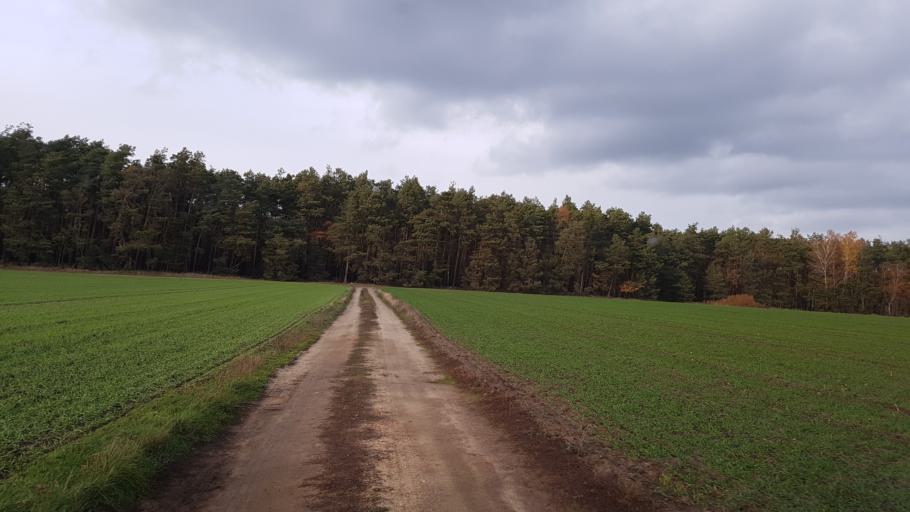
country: DE
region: Brandenburg
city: Schlieben
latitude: 51.6684
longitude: 13.4190
